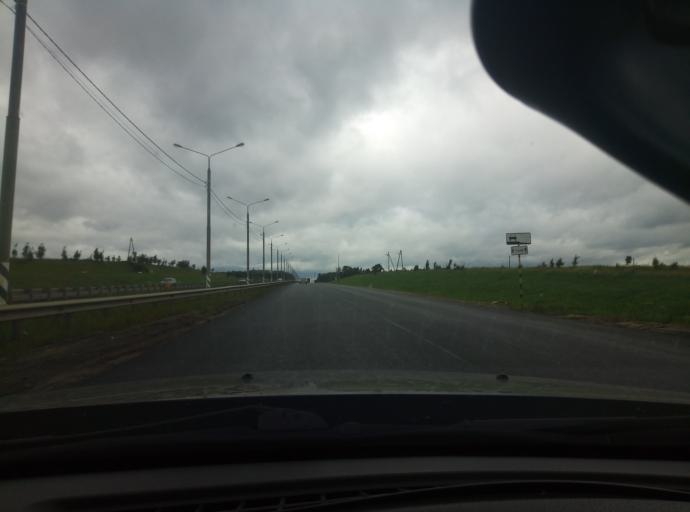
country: RU
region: Tula
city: Zaokskiy
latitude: 54.7354
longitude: 37.5049
